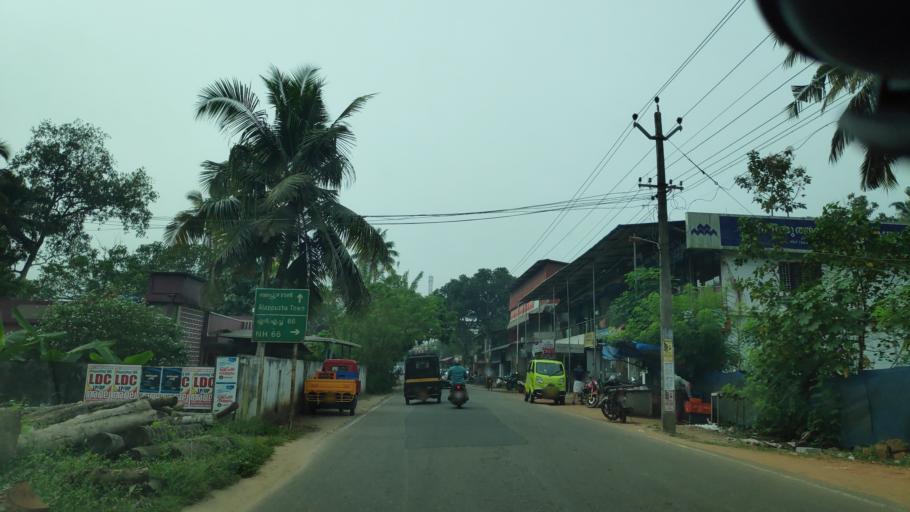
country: IN
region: Kerala
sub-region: Alappuzha
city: Alleppey
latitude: 9.5740
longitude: 76.3479
